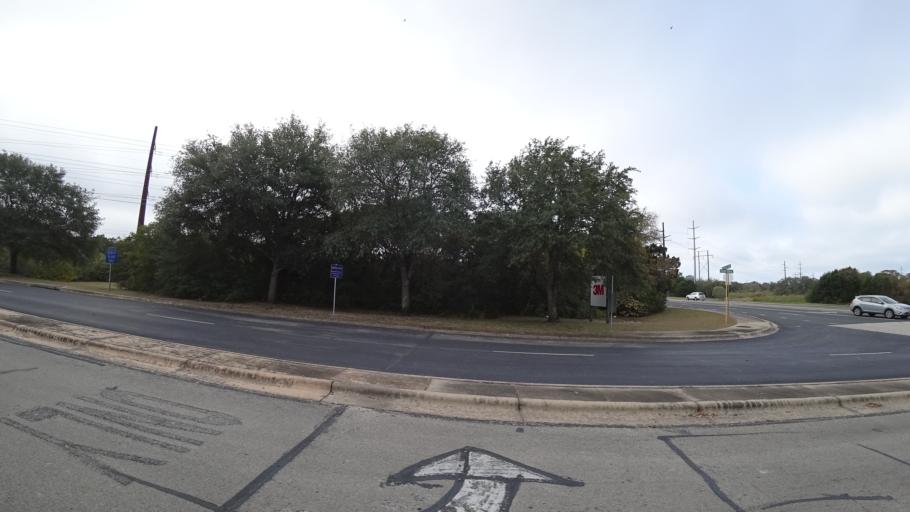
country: US
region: Texas
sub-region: Williamson County
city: Anderson Mill
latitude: 30.3988
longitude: -97.8446
